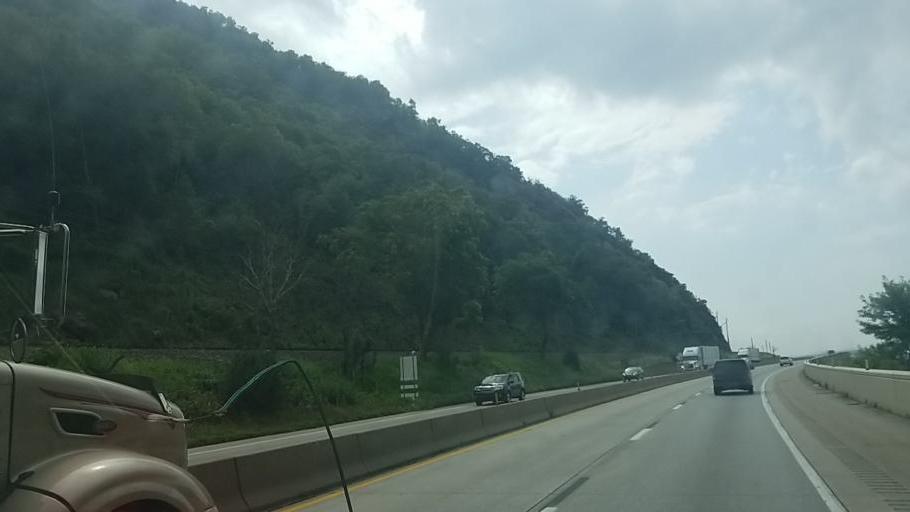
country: US
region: Pennsylvania
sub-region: Perry County
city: Marysville
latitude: 40.3605
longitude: -76.9256
